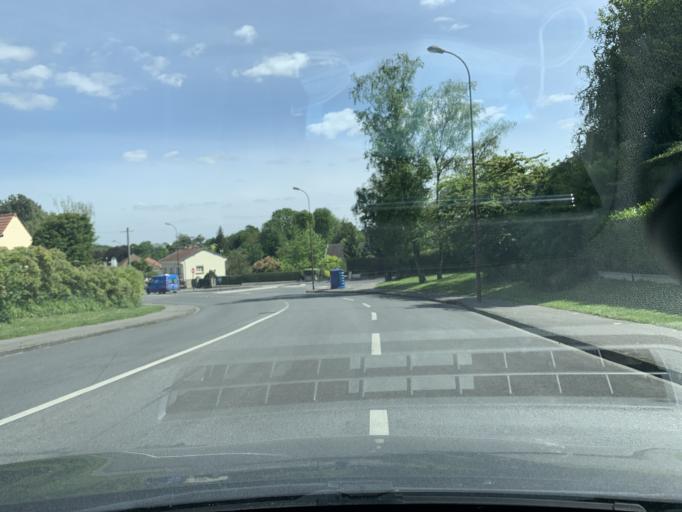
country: FR
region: Picardie
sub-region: Departement de l'Aisne
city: Saint-Quentin
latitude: 49.8585
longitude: 3.2958
